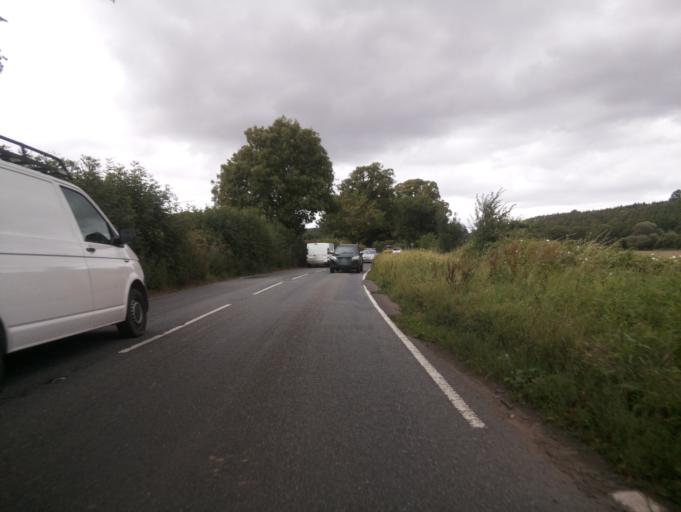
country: GB
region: England
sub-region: Devon
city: Starcross
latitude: 50.6458
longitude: -3.4780
